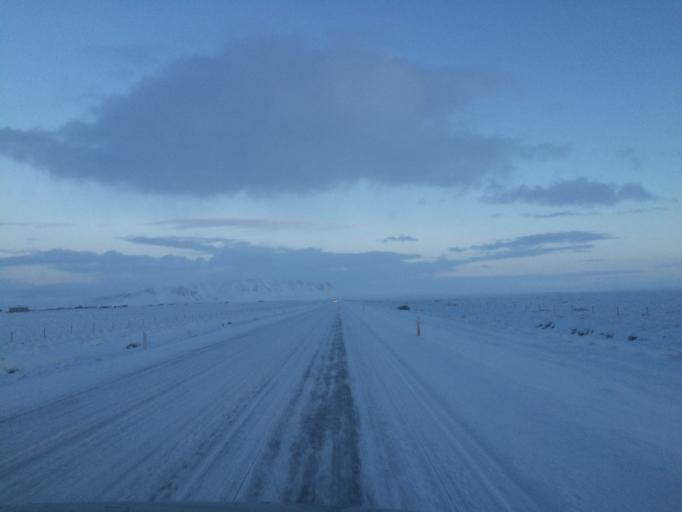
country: IS
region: South
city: Selfoss
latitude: 63.8788
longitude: -21.0900
